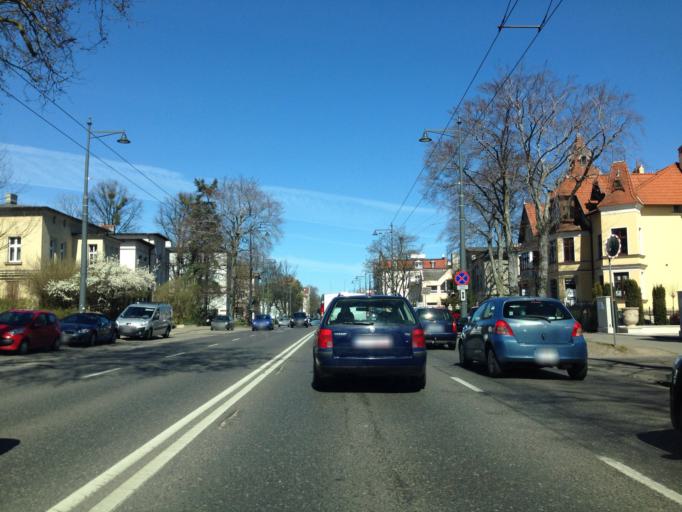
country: PL
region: Pomeranian Voivodeship
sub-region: Sopot
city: Sopot
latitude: 54.4369
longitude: 18.5611
